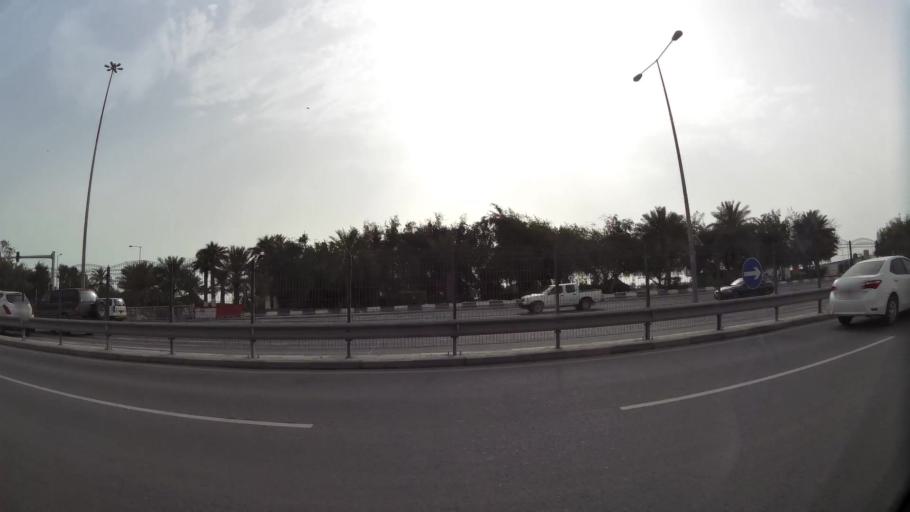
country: QA
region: Baladiyat ad Dawhah
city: Doha
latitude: 25.2733
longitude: 51.5525
